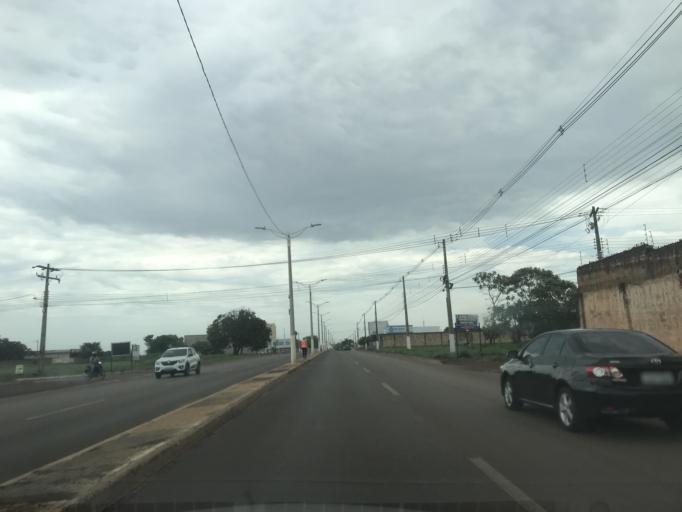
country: BR
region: Goias
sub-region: Luziania
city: Luziania
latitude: -16.2247
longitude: -47.9368
